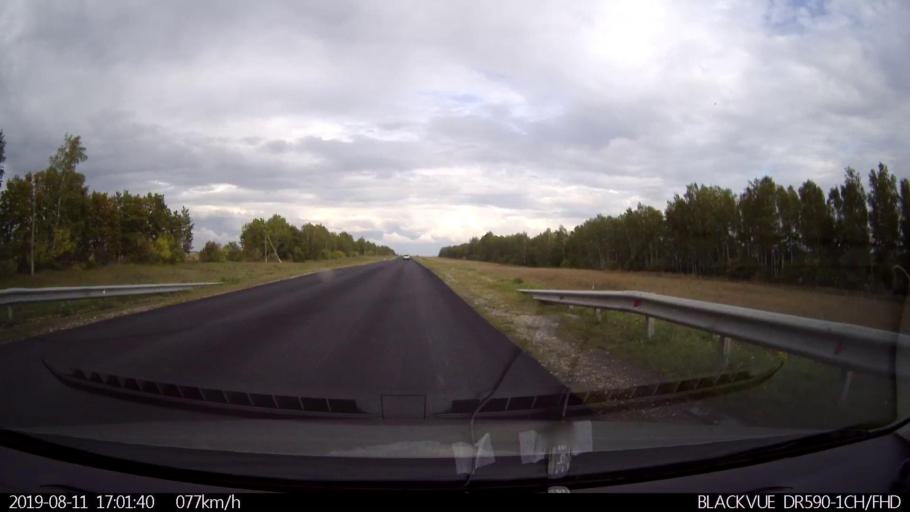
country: RU
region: Ulyanovsk
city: Mayna
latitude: 54.3076
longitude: 47.7018
